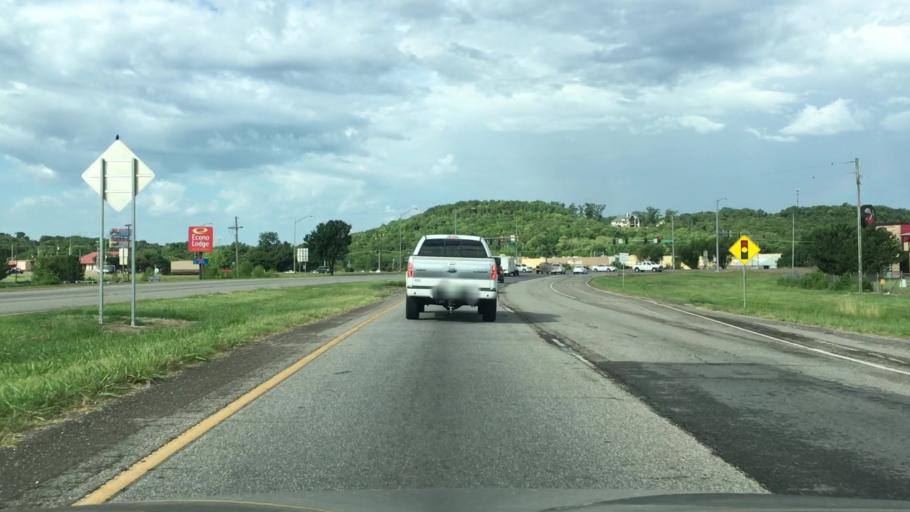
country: US
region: Oklahoma
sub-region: Cherokee County
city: Tahlequah
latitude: 35.8912
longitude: -94.9756
